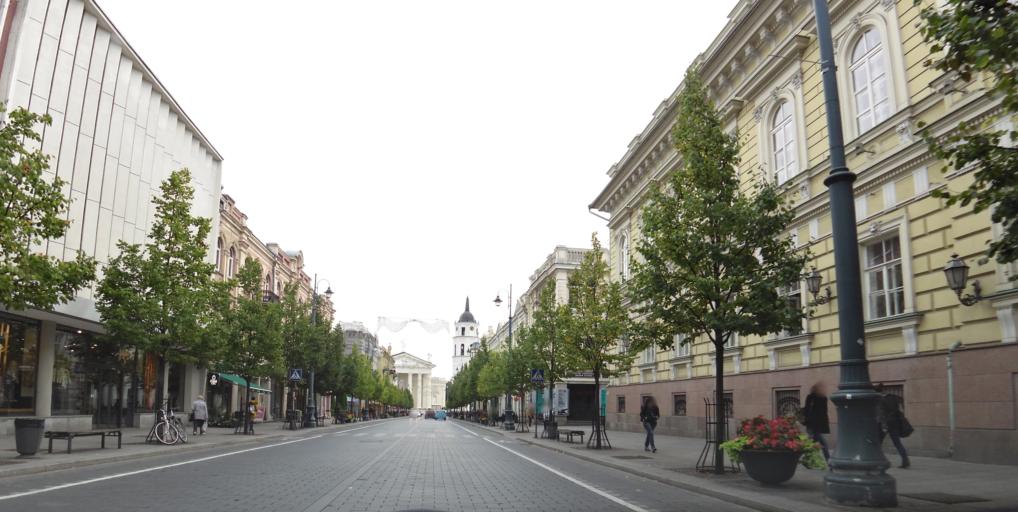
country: LT
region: Vilnius County
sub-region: Vilnius
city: Vilnius
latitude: 54.6865
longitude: 25.2832
